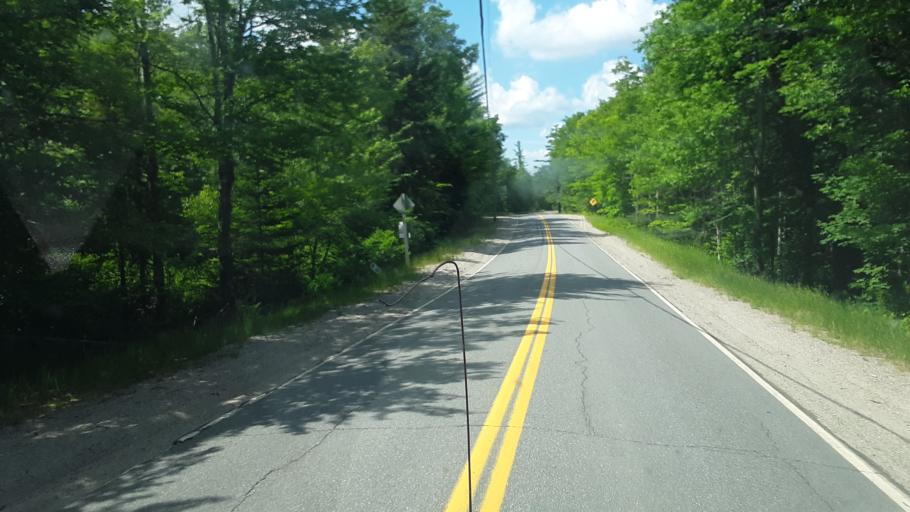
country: US
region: Maine
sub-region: Washington County
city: Machias
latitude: 44.9304
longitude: -67.6626
